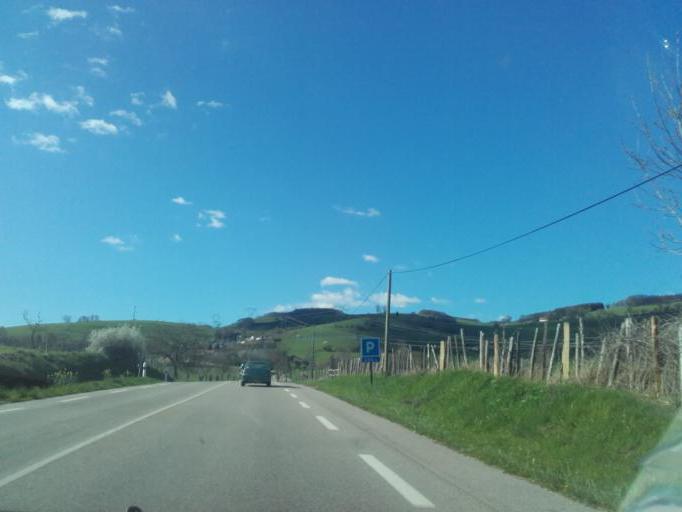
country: FR
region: Rhone-Alpes
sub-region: Departement de l'Isere
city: Saint-Hilaire-de-la-Cote
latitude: 45.3944
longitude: 5.3601
